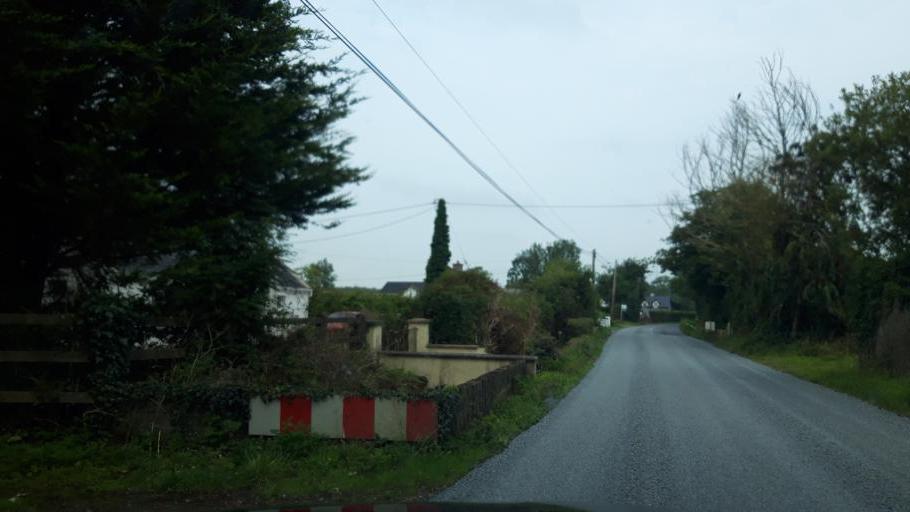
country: IE
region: Leinster
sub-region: Kilkenny
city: Callan
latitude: 52.5305
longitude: -7.5159
